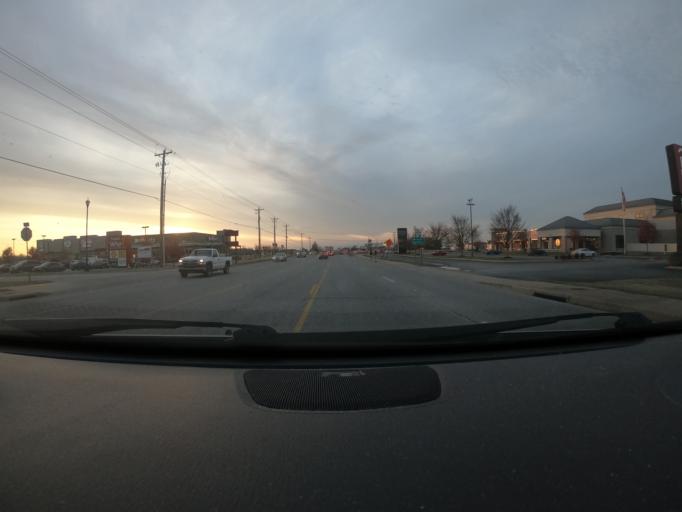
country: US
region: Arkansas
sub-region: Benton County
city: Bentonville
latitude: 36.3355
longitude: -94.2071
